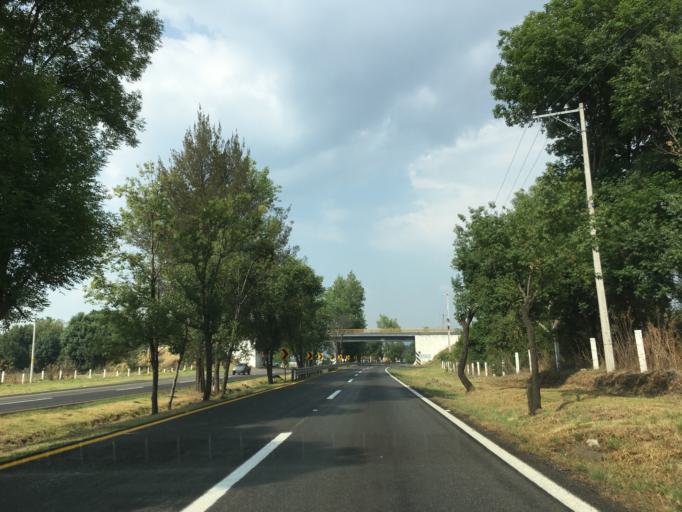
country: MX
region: Michoacan
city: Huiramba
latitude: 19.5442
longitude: -101.4510
